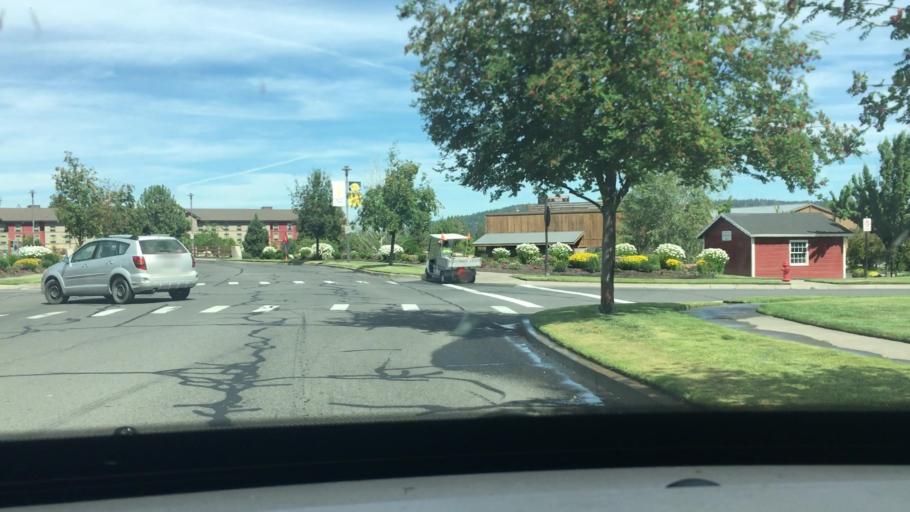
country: US
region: Oregon
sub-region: Deschutes County
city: Bend
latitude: 44.0428
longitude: -121.3152
